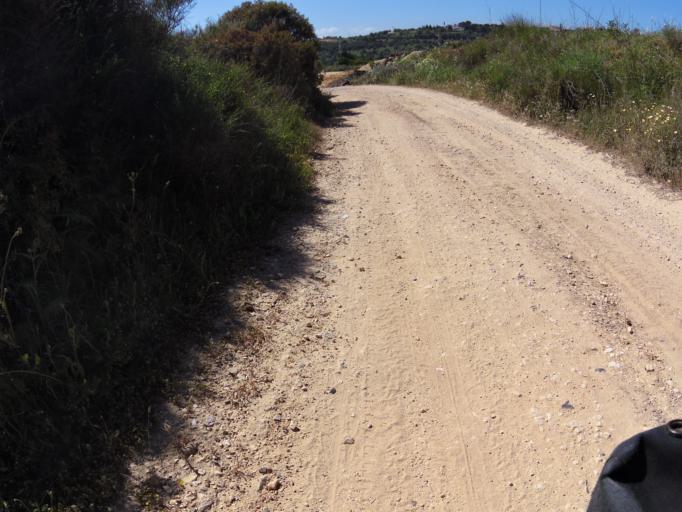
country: PT
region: Faro
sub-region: Lagos
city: Lagos
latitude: 37.0999
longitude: -8.7087
